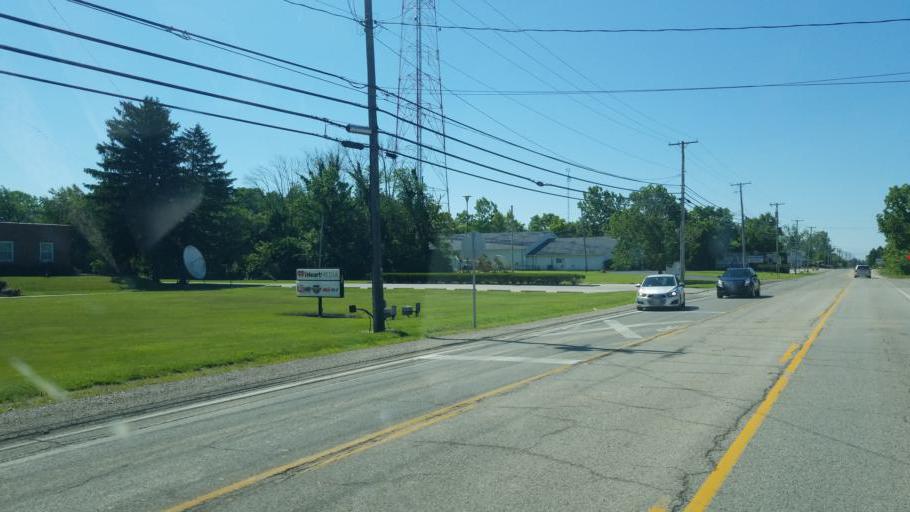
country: US
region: Ohio
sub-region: Marion County
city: Marion
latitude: 40.6142
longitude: -83.1312
